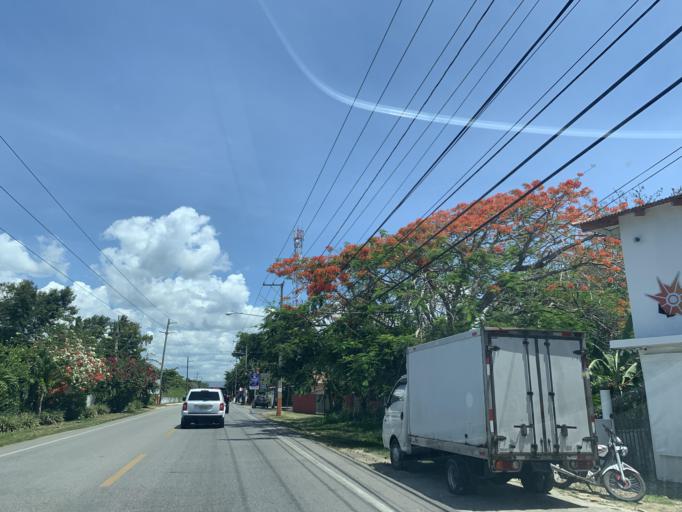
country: DO
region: Puerto Plata
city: Cabarete
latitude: 19.7327
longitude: -70.3888
